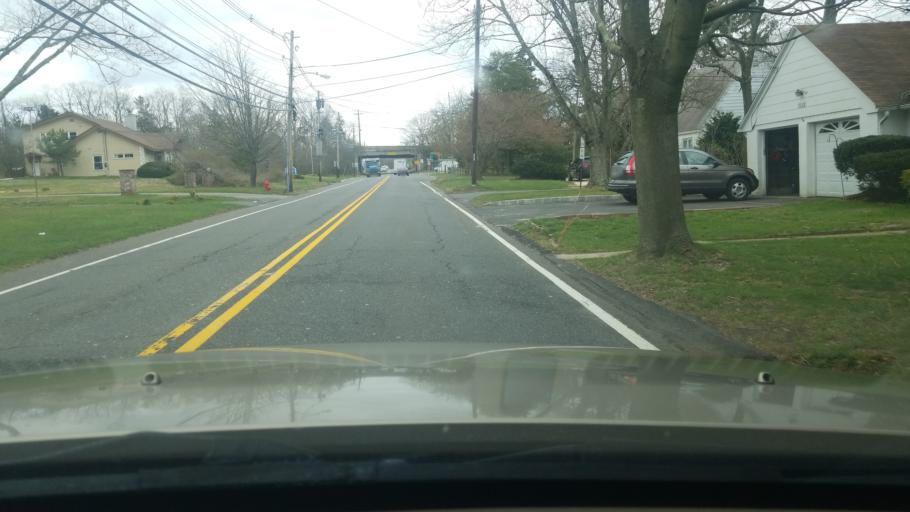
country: US
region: New Jersey
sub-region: Monmouth County
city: Manasquan
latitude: 40.1412
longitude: -74.0945
